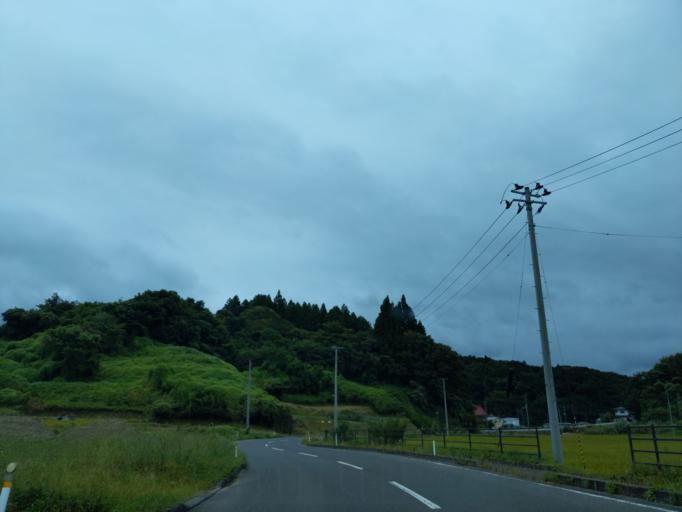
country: JP
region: Fukushima
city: Miharu
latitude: 37.3676
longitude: 140.5281
